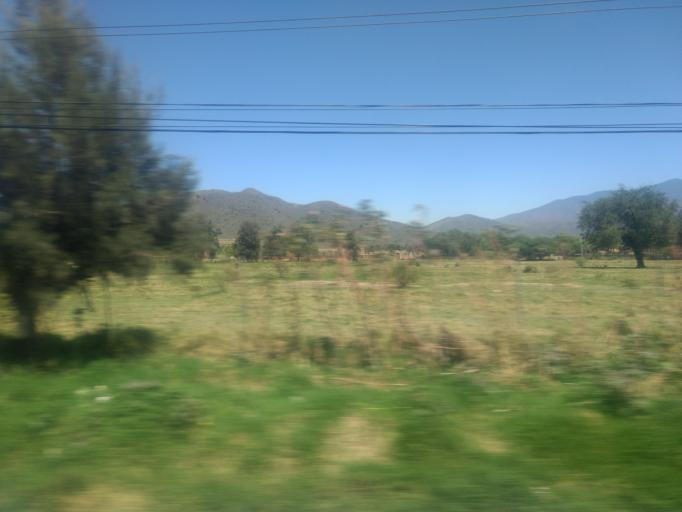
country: MX
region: Jalisco
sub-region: Tlajomulco de Zuniga
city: Santa Cruz de las Flores
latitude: 20.4866
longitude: -103.4934
